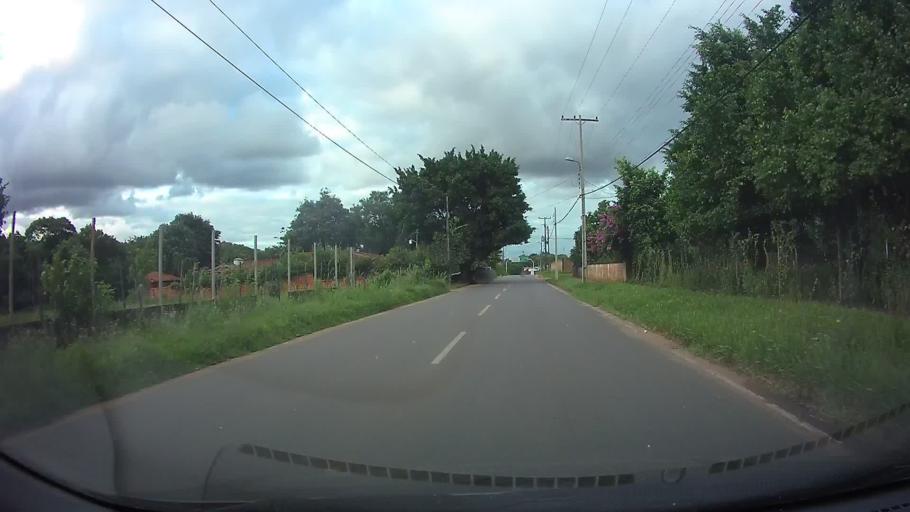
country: PY
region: Central
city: Fernando de la Mora
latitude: -25.2990
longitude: -57.5199
